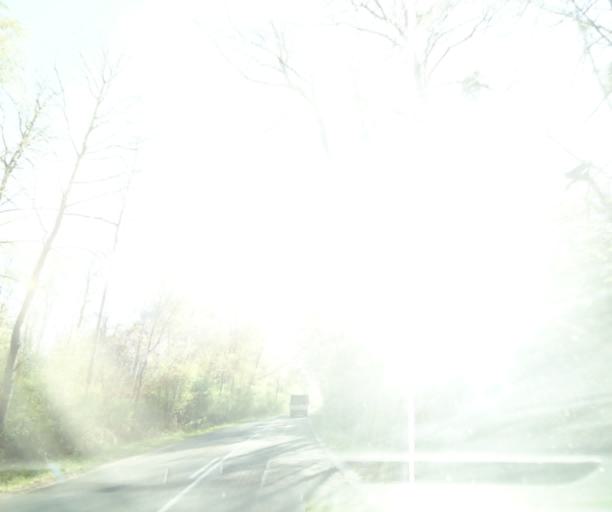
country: FR
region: Ile-de-France
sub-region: Departement de Seine-et-Marne
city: La Chapelle-Gauthier
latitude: 48.4968
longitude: 2.9038
